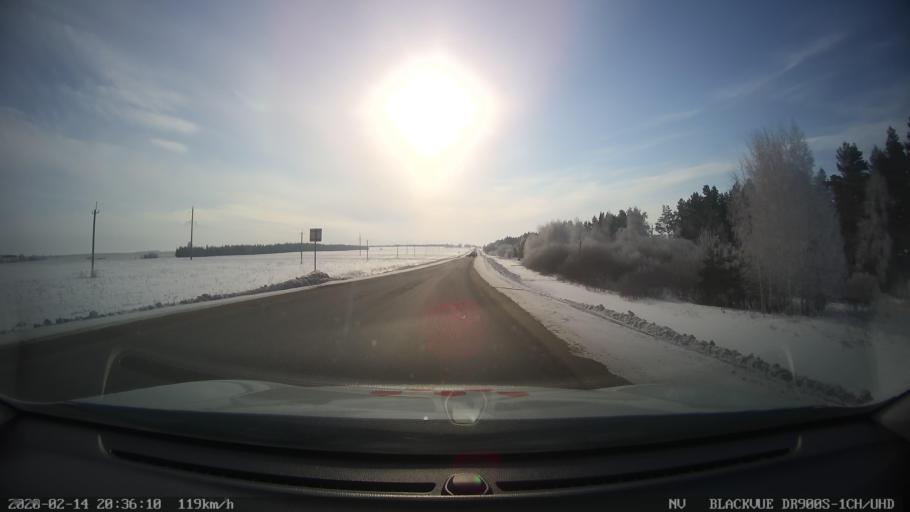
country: RU
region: Tatarstan
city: Kuybyshevskiy Zaton
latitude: 55.3732
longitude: 48.9960
